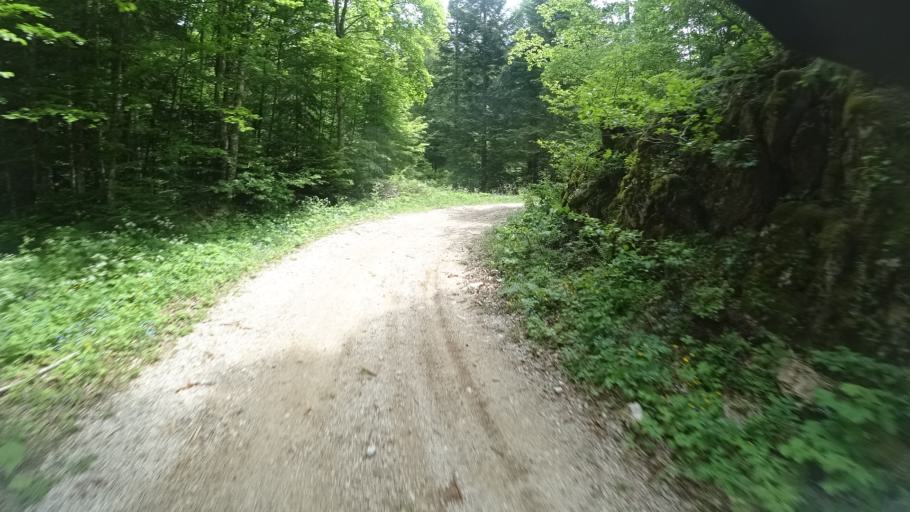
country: HR
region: Zadarska
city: Gracac
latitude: 44.4817
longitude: 15.8814
